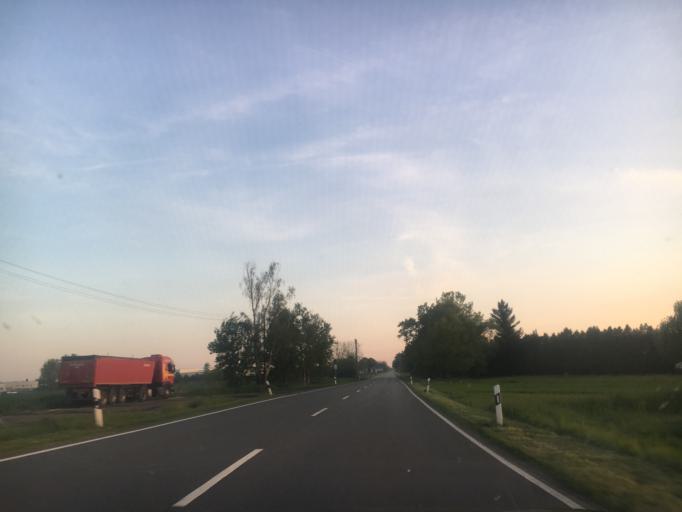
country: DE
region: Thuringia
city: Hirschfeld
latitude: 50.9644
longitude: 12.1324
